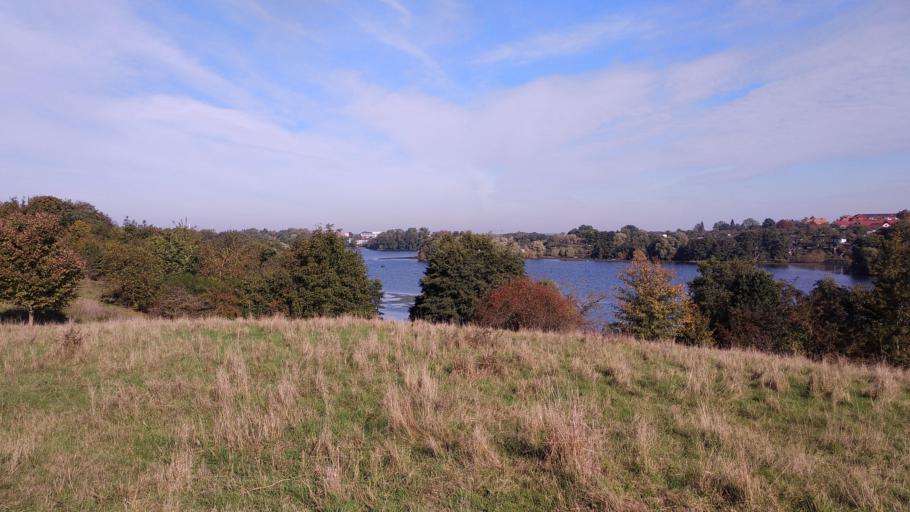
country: DE
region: Mecklenburg-Vorpommern
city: Neumuehle
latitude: 53.6346
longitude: 11.3797
